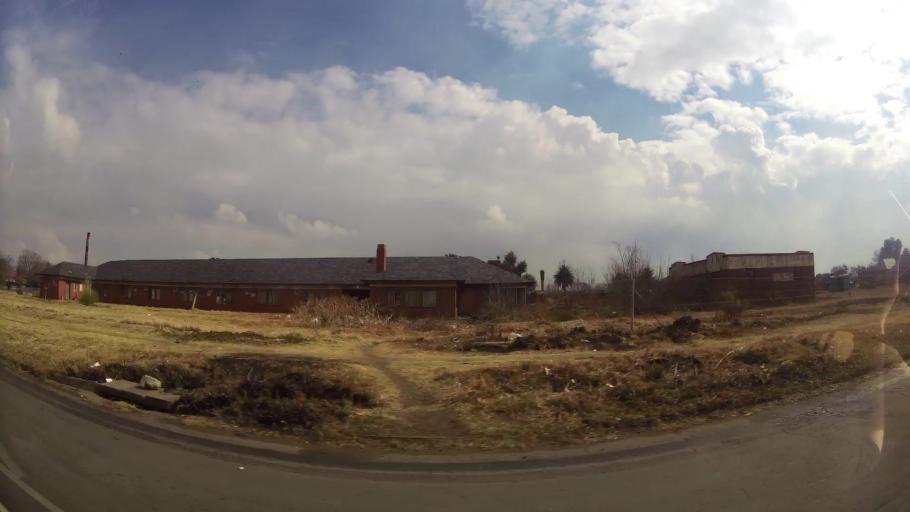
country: ZA
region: Gauteng
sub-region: Sedibeng District Municipality
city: Vereeniging
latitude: -26.6688
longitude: 27.9197
